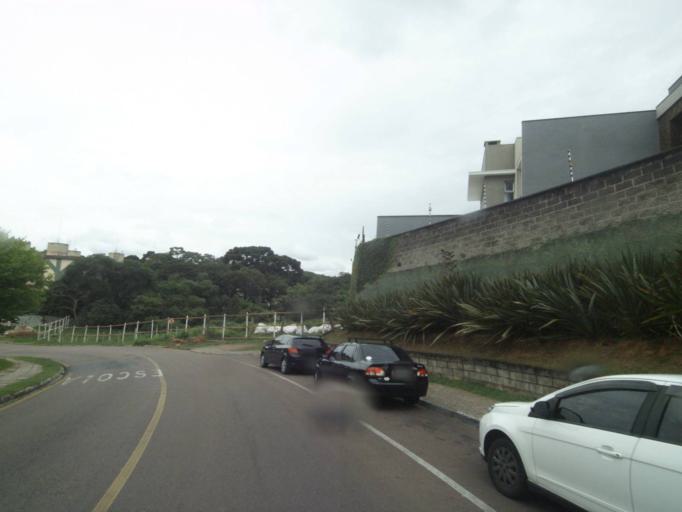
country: BR
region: Parana
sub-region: Curitiba
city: Curitiba
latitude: -25.4618
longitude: -49.3341
